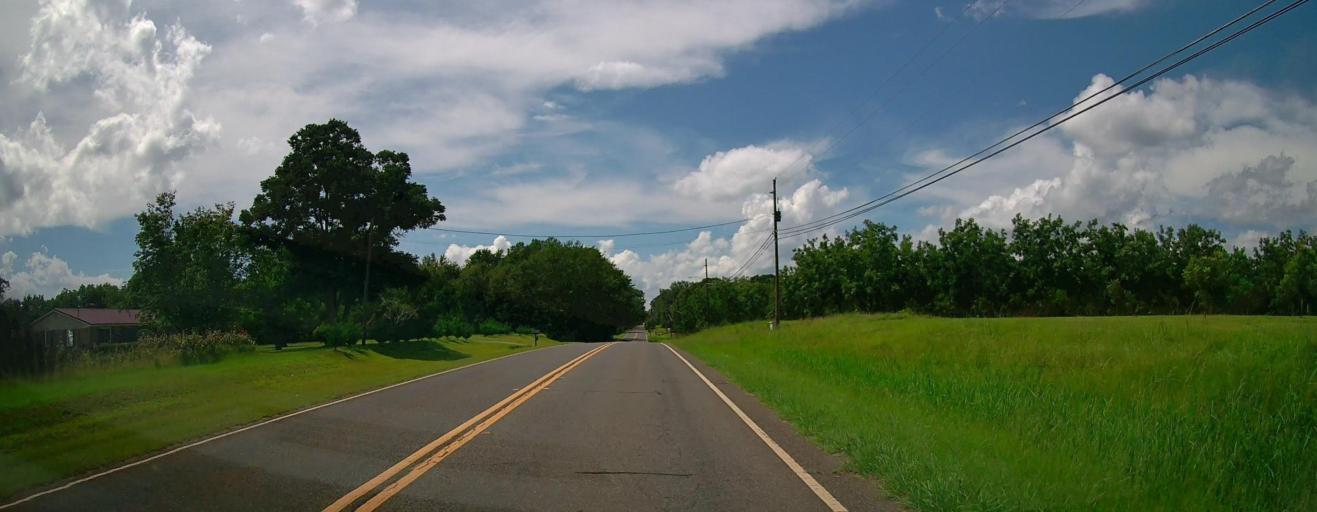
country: US
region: Georgia
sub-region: Macon County
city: Marshallville
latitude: 32.4562
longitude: -83.9293
